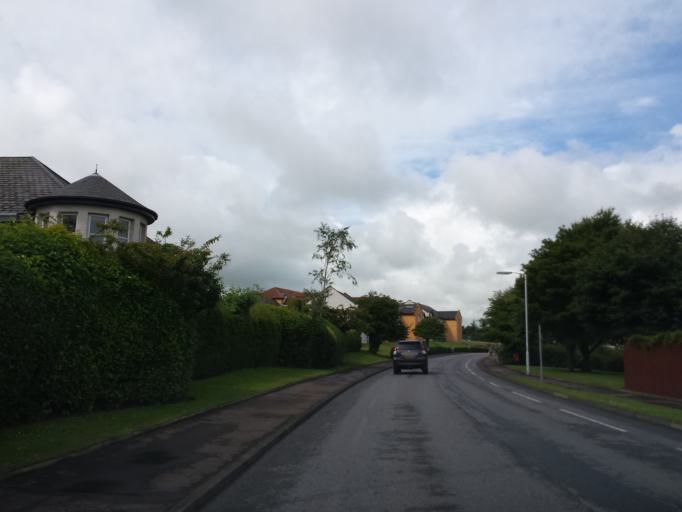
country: GB
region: Scotland
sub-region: Fife
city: Saint Andrews
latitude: 56.3281
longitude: -2.8101
